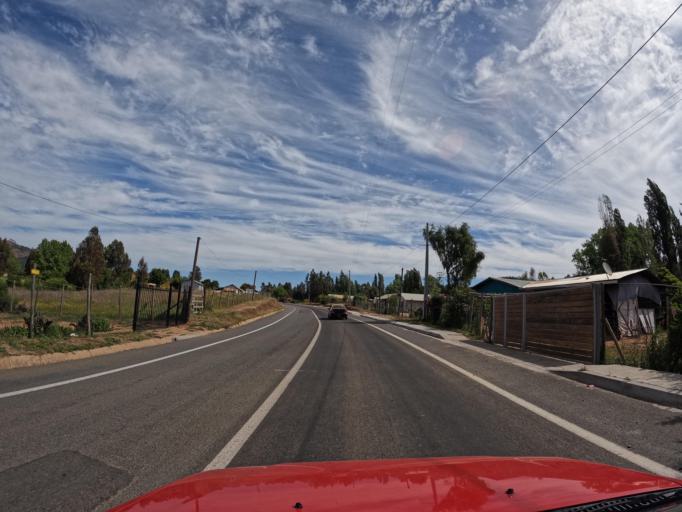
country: CL
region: Maule
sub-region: Provincia de Talca
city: Talca
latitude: -35.1169
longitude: -71.9582
